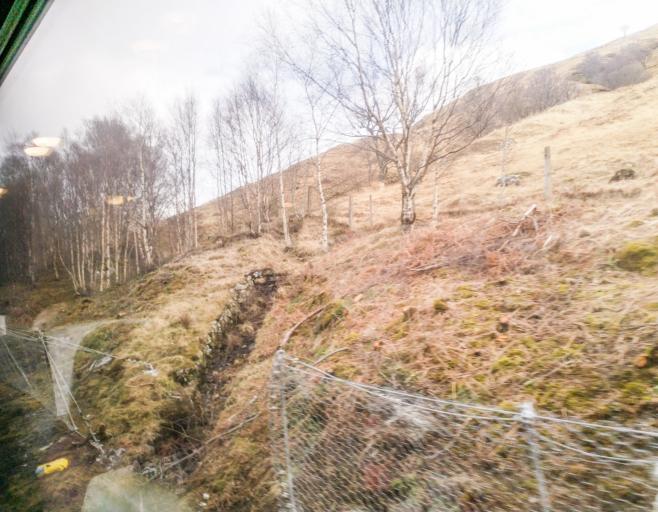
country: GB
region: Scotland
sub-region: Highland
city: Spean Bridge
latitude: 56.7996
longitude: -4.7211
